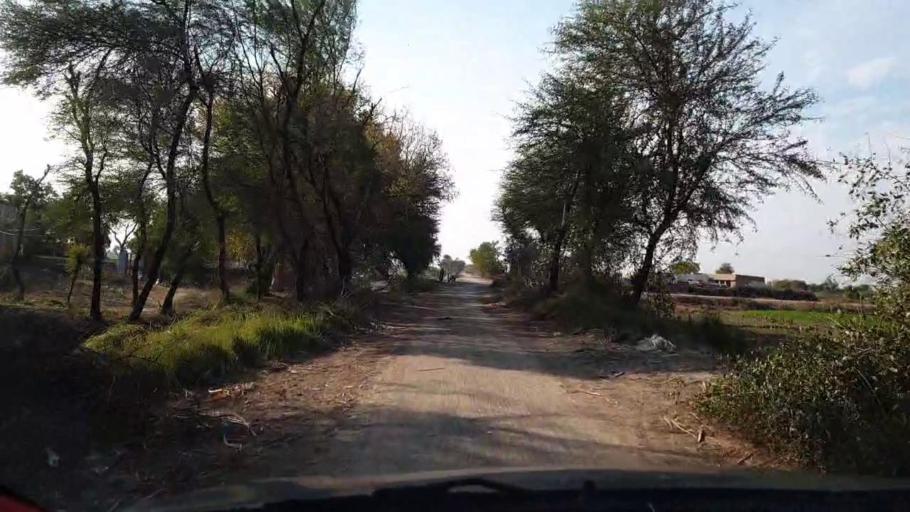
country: PK
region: Sindh
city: Sinjhoro
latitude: 25.9751
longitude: 68.8261
